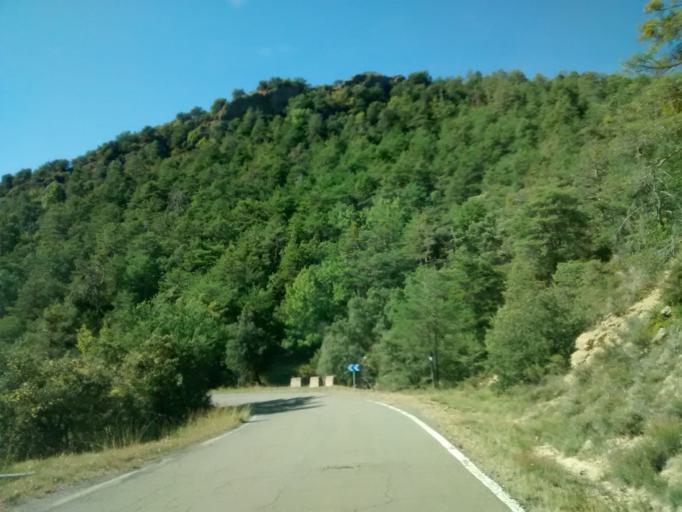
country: ES
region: Aragon
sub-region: Provincia de Huesca
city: Jaca
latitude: 42.4861
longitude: -0.5664
